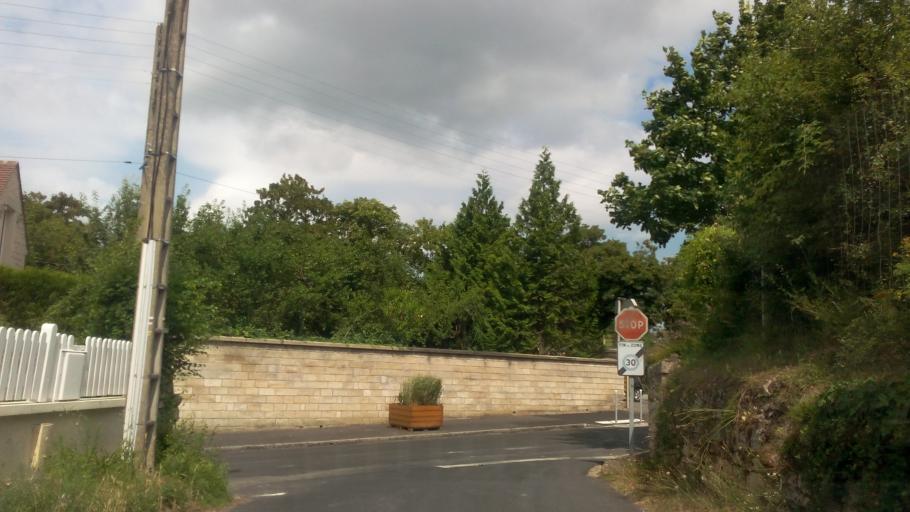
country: FR
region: Picardie
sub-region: Departement de l'Oise
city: Saint-Maximin
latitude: 49.2207
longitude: 2.4471
